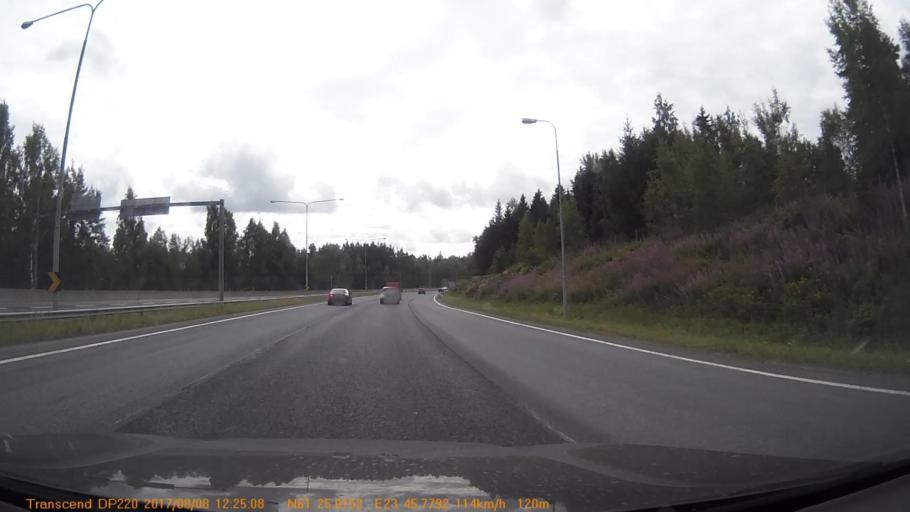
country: FI
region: Pirkanmaa
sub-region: Tampere
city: Tampere
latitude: 61.4168
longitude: 23.7632
